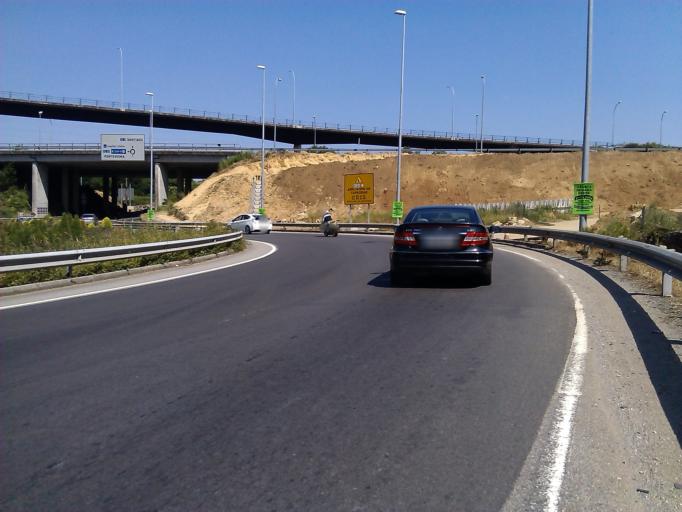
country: ES
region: Galicia
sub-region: Provincia da Coruna
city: Santiago de Compostela
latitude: 42.8552
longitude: -8.5306
